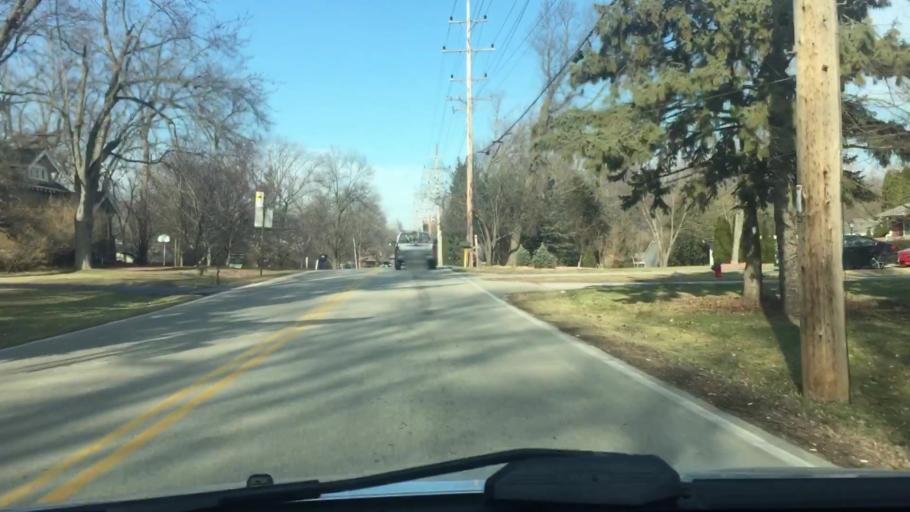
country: US
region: Wisconsin
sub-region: Waukesha County
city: Elm Grove
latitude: 43.0462
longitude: -88.0669
